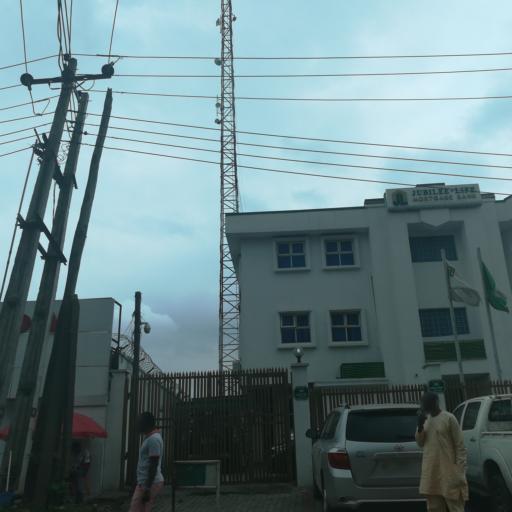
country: NG
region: Lagos
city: Ikeja
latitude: 6.6122
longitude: 3.3454
